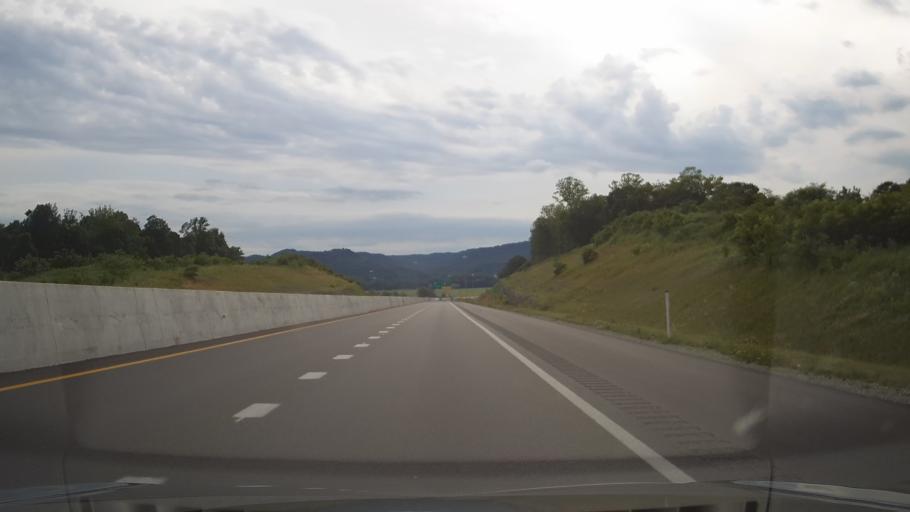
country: US
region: Ohio
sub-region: Scioto County
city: Lucasville
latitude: 38.8920
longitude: -82.9904
